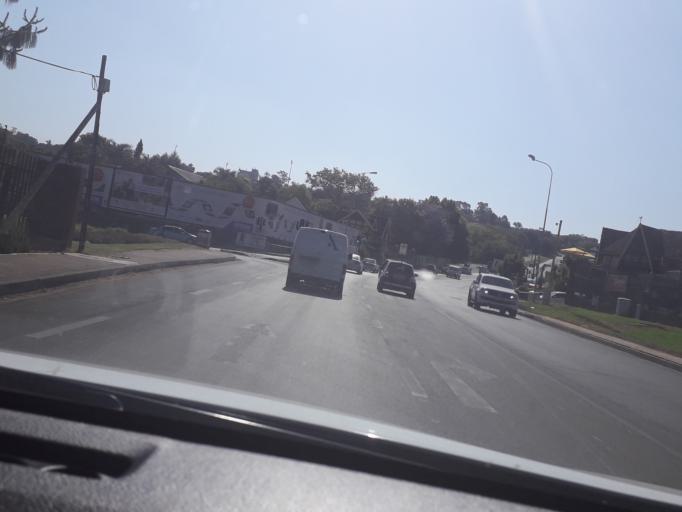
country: ZA
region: Gauteng
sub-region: City of Johannesburg Metropolitan Municipality
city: Johannesburg
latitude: -26.0818
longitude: 28.0187
